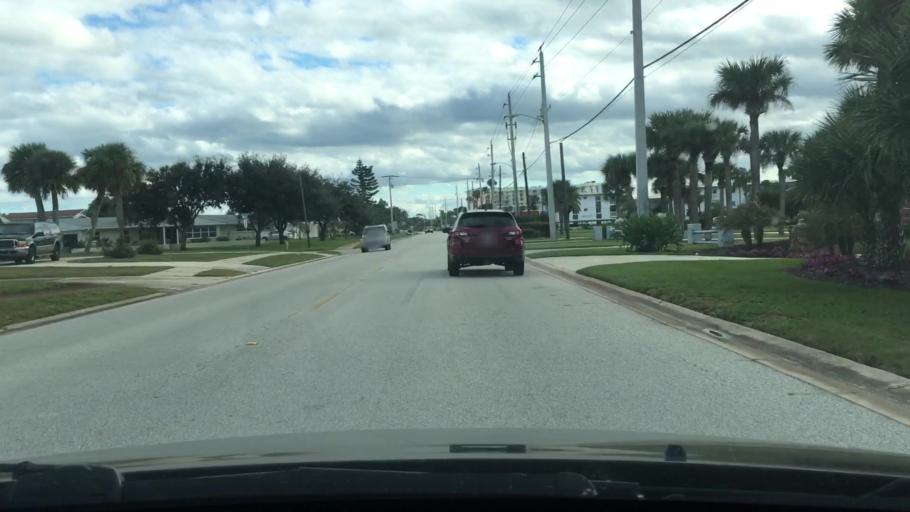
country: US
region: Florida
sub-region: Volusia County
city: Holly Hill
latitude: 29.2668
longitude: -81.0364
